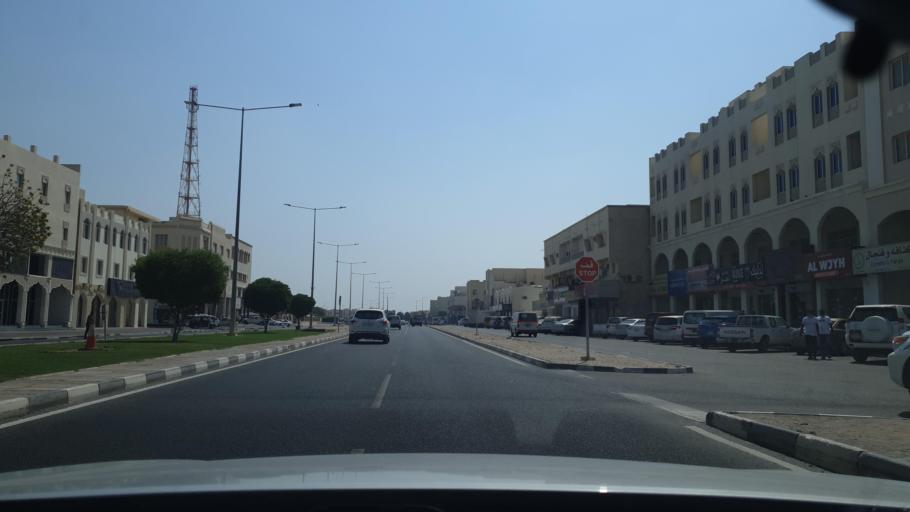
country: QA
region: Al Khawr
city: Al Khawr
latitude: 25.6851
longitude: 51.4954
